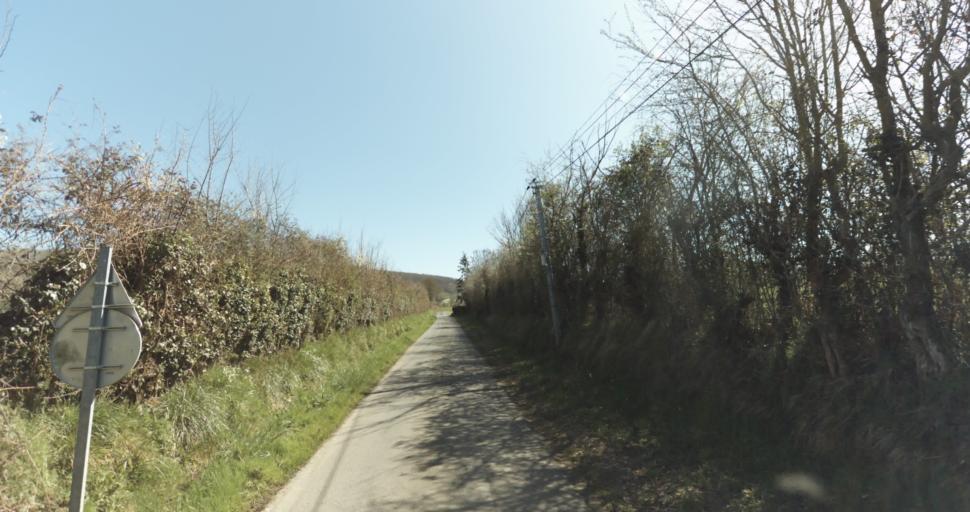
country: FR
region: Lower Normandy
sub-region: Departement du Calvados
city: Saint-Pierre-sur-Dives
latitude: 49.0085
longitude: 0.0280
